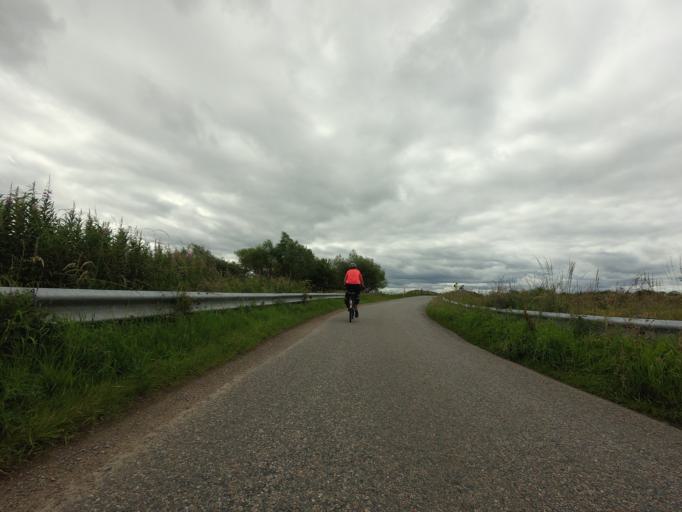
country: GB
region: Scotland
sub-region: Moray
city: Forres
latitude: 57.6251
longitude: -3.6070
